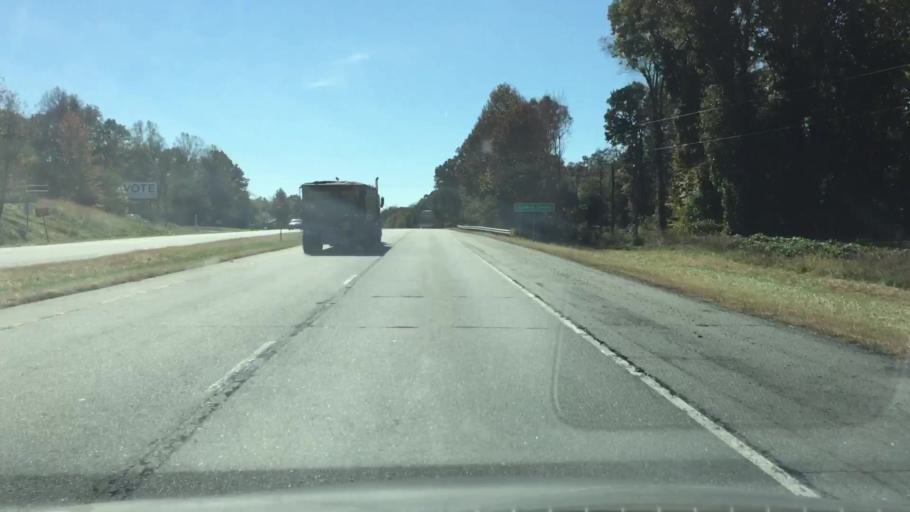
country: US
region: North Carolina
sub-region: Rockingham County
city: Reidsville
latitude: 36.2449
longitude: -79.6670
